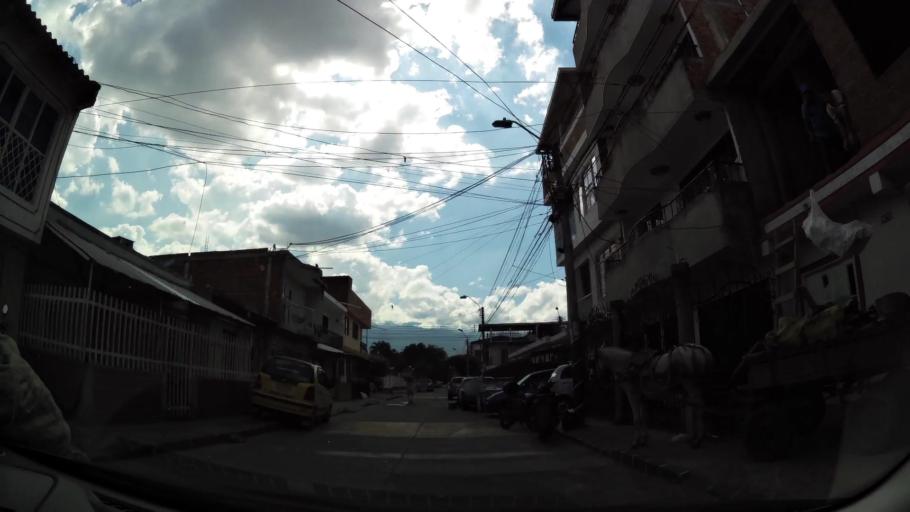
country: CO
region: Valle del Cauca
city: Cali
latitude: 3.4161
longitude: -76.5185
